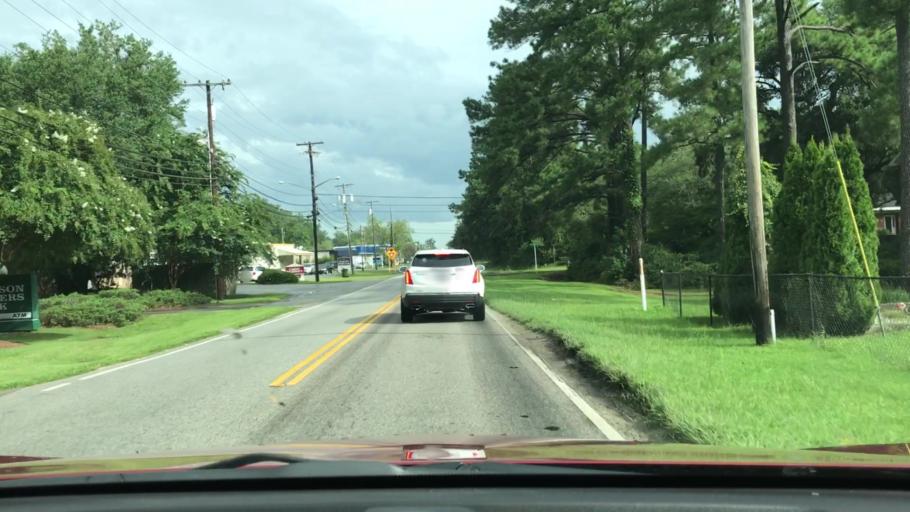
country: US
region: South Carolina
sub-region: Georgetown County
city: Georgetown
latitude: 33.3810
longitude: -79.2862
